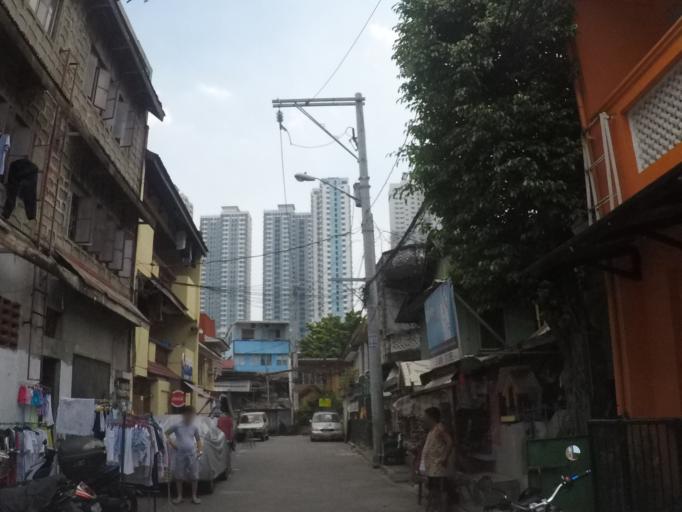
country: PH
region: Metro Manila
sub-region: San Juan
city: San Juan
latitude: 14.6048
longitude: 121.0215
